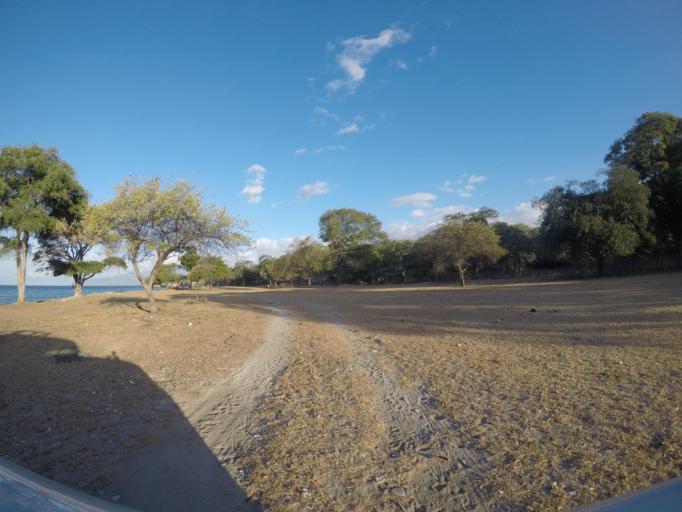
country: TL
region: Lautem
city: Lospalos
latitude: -8.3258
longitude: 127.0054
